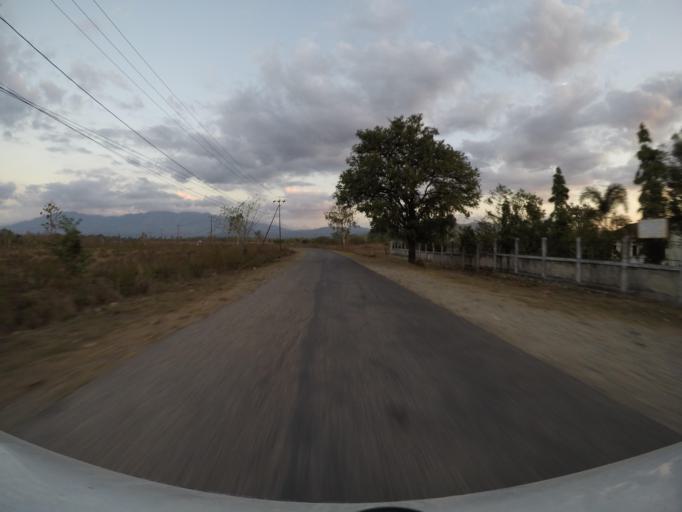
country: TL
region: Bobonaro
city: Maliana
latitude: -8.9684
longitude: 125.1289
